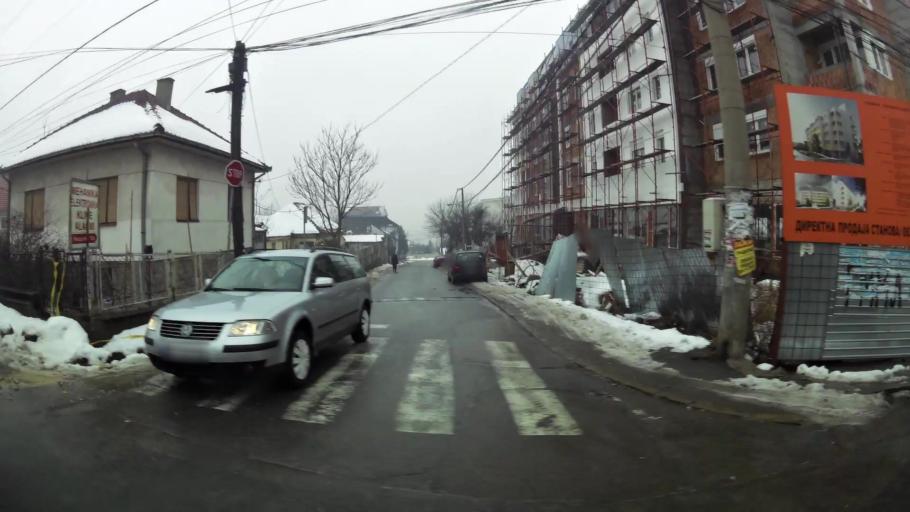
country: RS
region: Central Serbia
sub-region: Belgrade
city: Zvezdara
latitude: 44.7812
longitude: 20.5229
